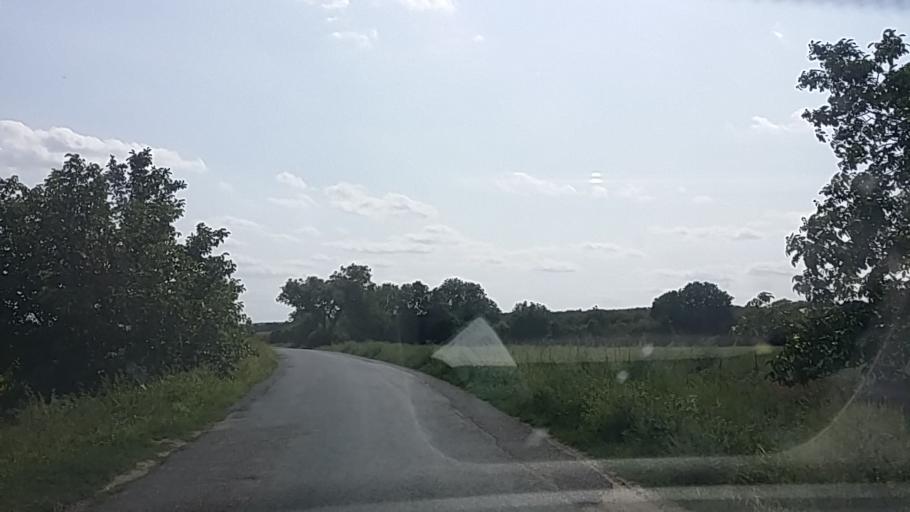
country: HU
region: Gyor-Moson-Sopron
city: Fertorakos
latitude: 47.7101
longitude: 16.6566
